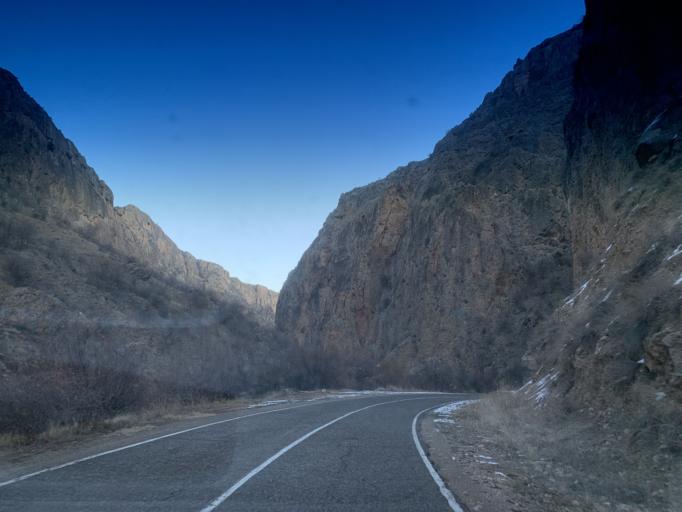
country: AM
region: Vayots' Dzori Marz
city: Areni
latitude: 39.7154
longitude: 45.2061
